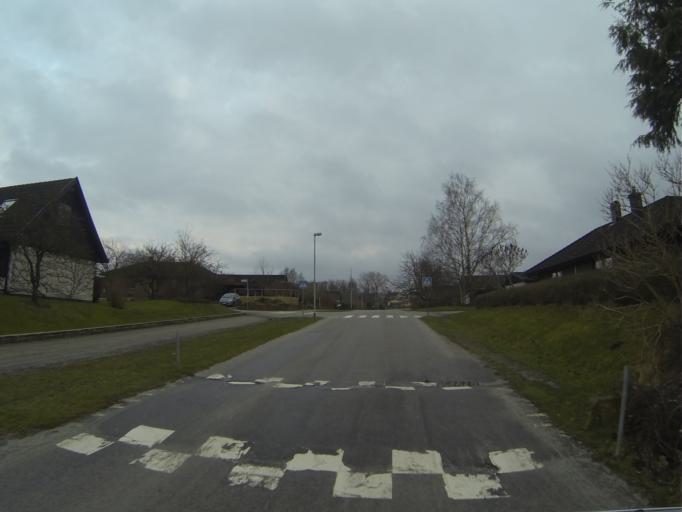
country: SE
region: Skane
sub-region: Lunds Kommun
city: Genarp
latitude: 55.7110
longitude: 13.3328
